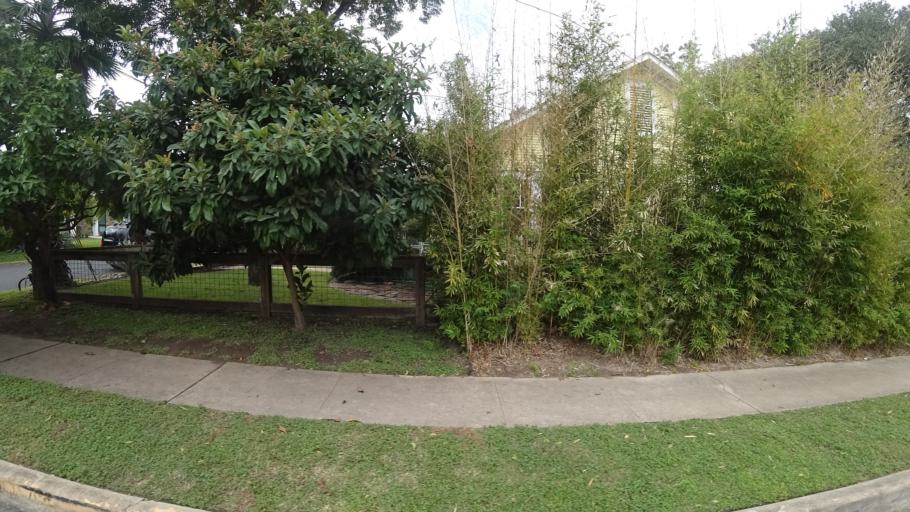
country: US
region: Texas
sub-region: Travis County
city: Austin
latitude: 30.2532
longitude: -97.7573
